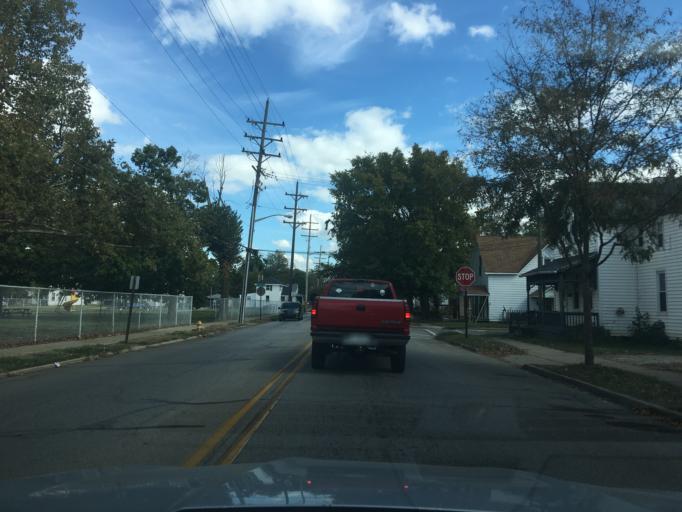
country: US
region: Indiana
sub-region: Tippecanoe County
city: Lafayette
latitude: 40.4320
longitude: -86.8828
